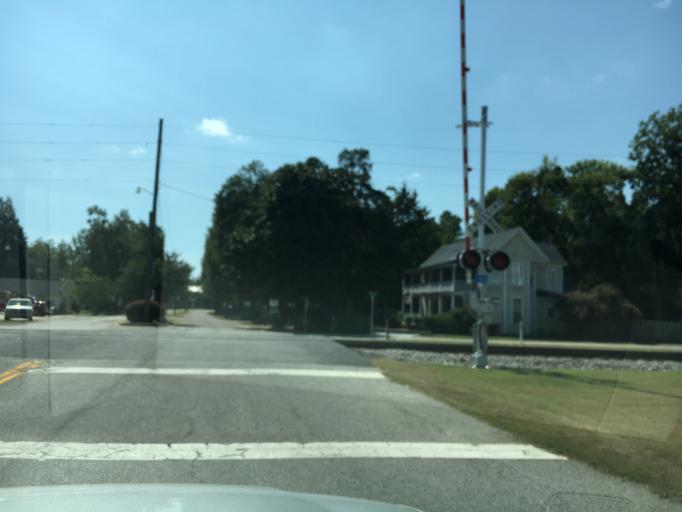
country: US
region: South Carolina
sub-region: Lexington County
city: Batesburg
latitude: 33.8453
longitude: -81.6619
